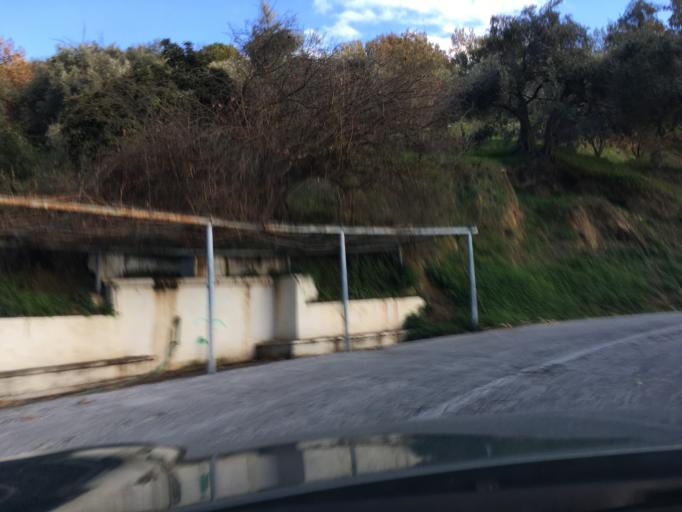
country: GR
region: Thessaly
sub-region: Nomos Magnisias
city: Skopelos
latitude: 39.1715
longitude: 23.6165
